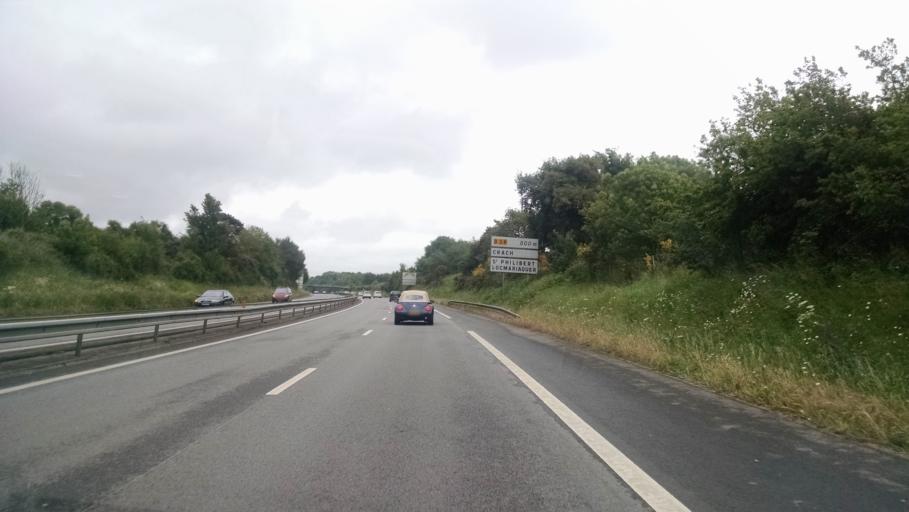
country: FR
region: Brittany
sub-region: Departement du Morbihan
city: Auray
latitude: 47.6591
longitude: -3.0045
